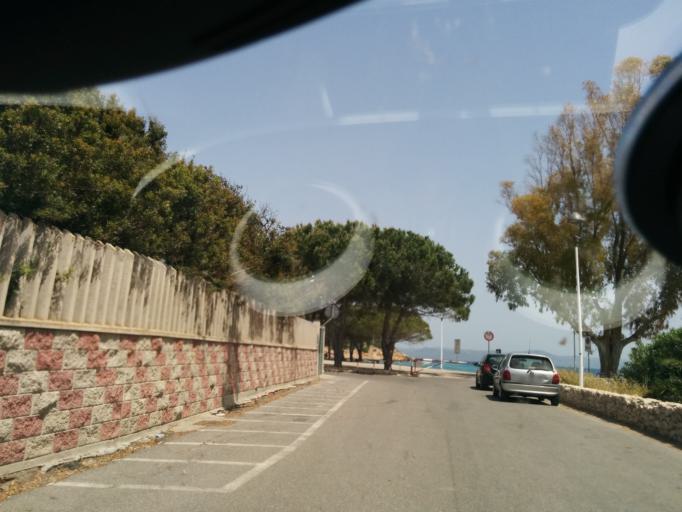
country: IT
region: Sardinia
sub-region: Provincia di Carbonia-Iglesias
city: Sant'Antioco
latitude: 38.9986
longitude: 8.4483
